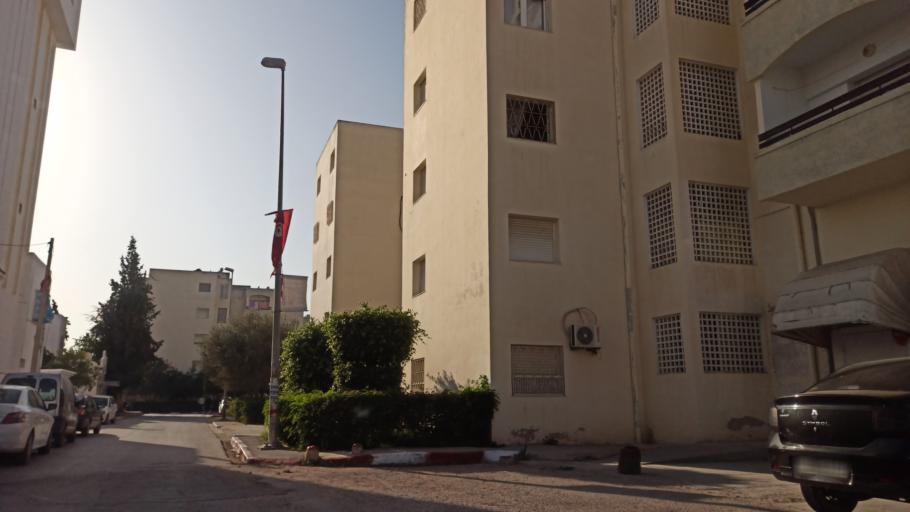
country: TN
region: Tunis
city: La Goulette
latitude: 36.8558
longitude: 10.2698
